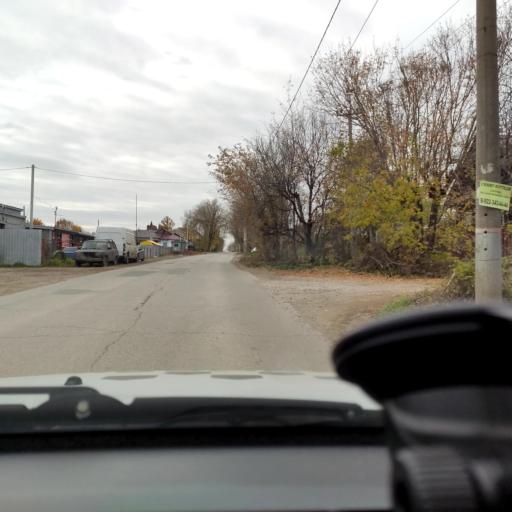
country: RU
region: Perm
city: Perm
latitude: 57.9958
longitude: 56.3126
